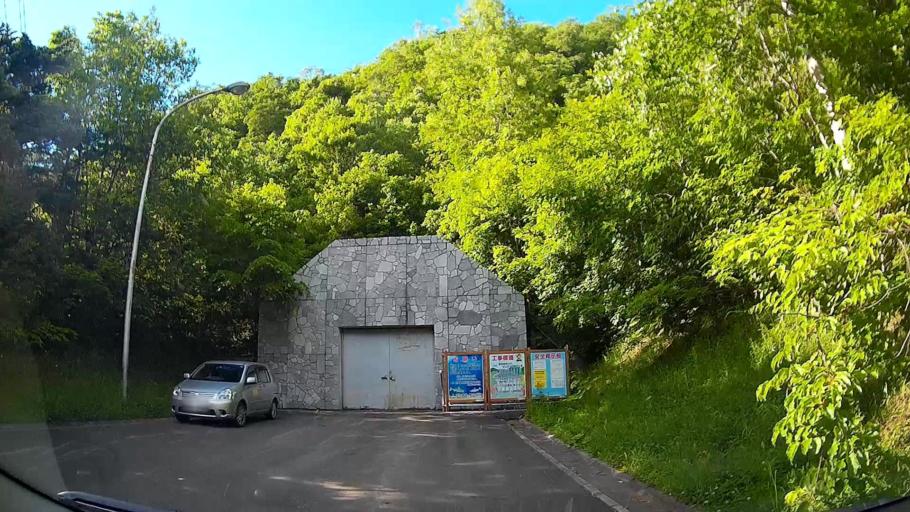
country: JP
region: Hokkaido
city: Sapporo
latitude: 42.9822
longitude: 141.1593
